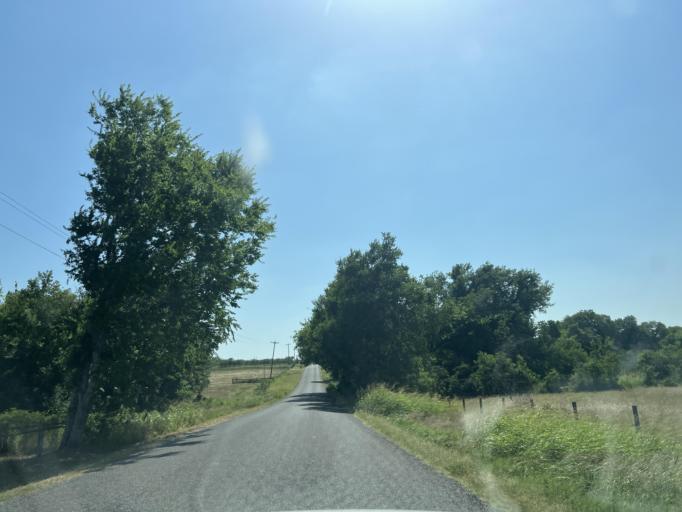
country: US
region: Texas
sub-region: Washington County
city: Brenham
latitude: 30.1593
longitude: -96.3404
